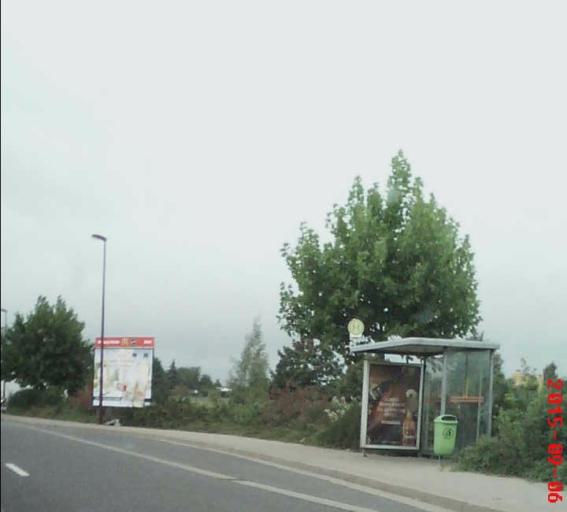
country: DE
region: Thuringia
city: Muehlhausen
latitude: 51.2143
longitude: 10.4668
